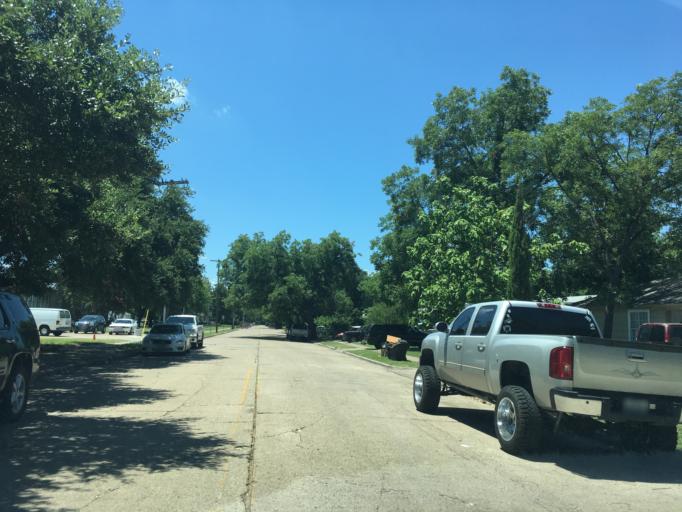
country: US
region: Texas
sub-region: Dallas County
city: Garland
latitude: 32.8470
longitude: -96.6760
